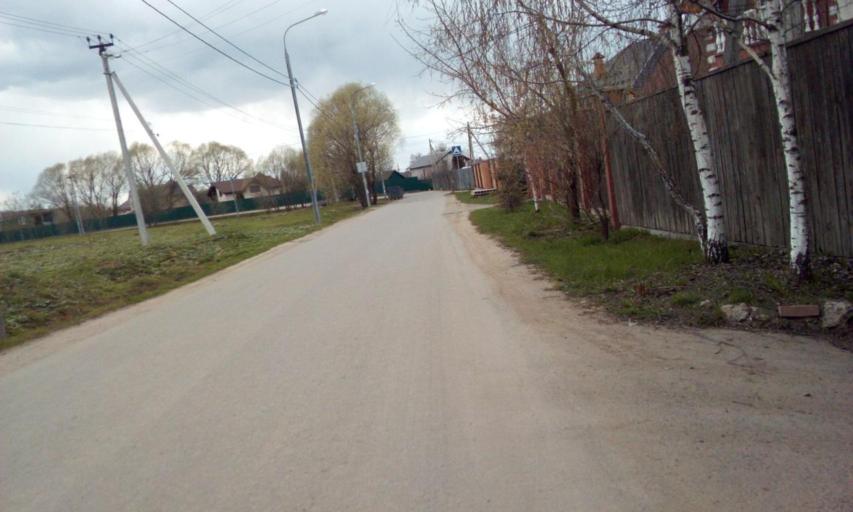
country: RU
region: Moskovskaya
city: Kommunarka
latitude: 55.5241
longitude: 37.4833
